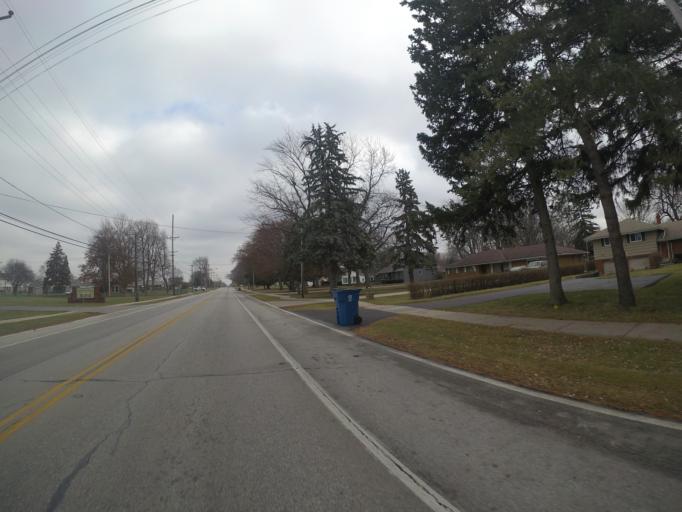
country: US
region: Ohio
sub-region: Lucas County
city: Oregon
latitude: 41.6441
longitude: -83.4802
